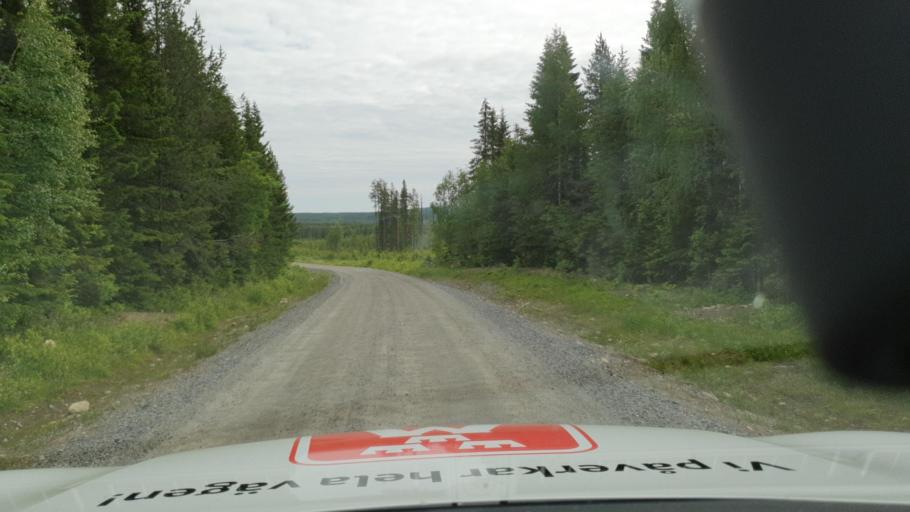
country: SE
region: Vaesterbotten
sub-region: Skelleftea Kommun
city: Langsele
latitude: 64.6471
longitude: 20.3109
